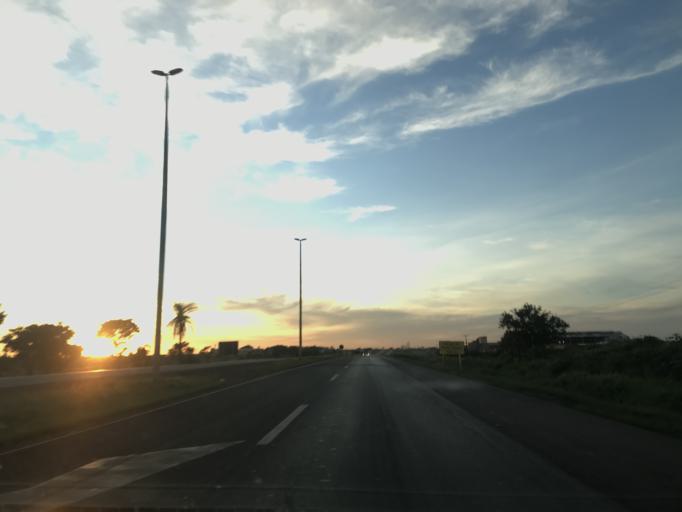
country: BR
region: Goias
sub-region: Luziania
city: Luziania
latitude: -16.2486
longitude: -47.9038
